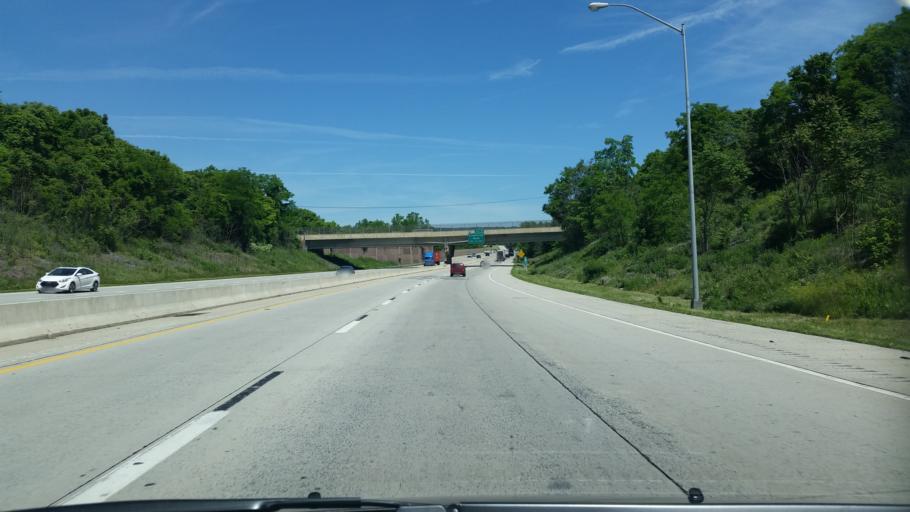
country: US
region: Pennsylvania
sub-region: Cumberland County
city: Shiremanstown
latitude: 40.2490
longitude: -76.9855
